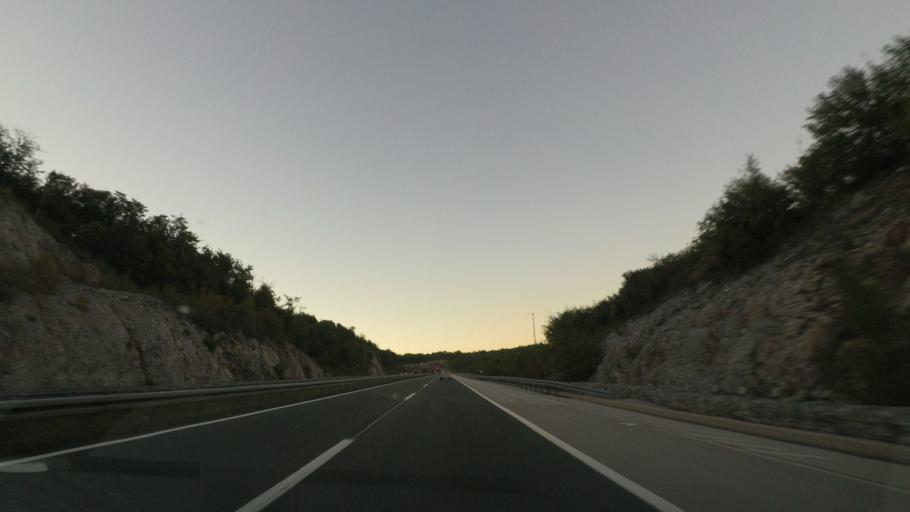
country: HR
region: Zadarska
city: Obrovac
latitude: 44.3583
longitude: 15.6404
